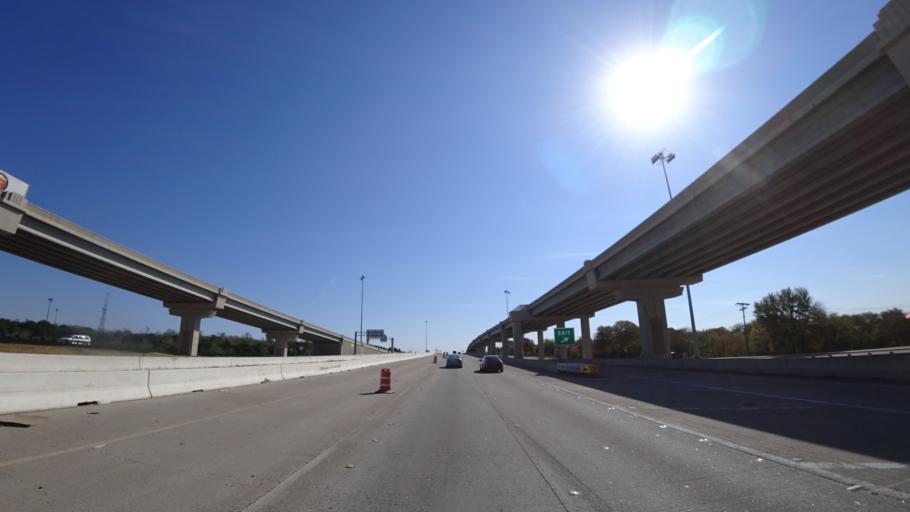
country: US
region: Texas
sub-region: Travis County
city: Austin
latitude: 30.3231
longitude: -97.6703
